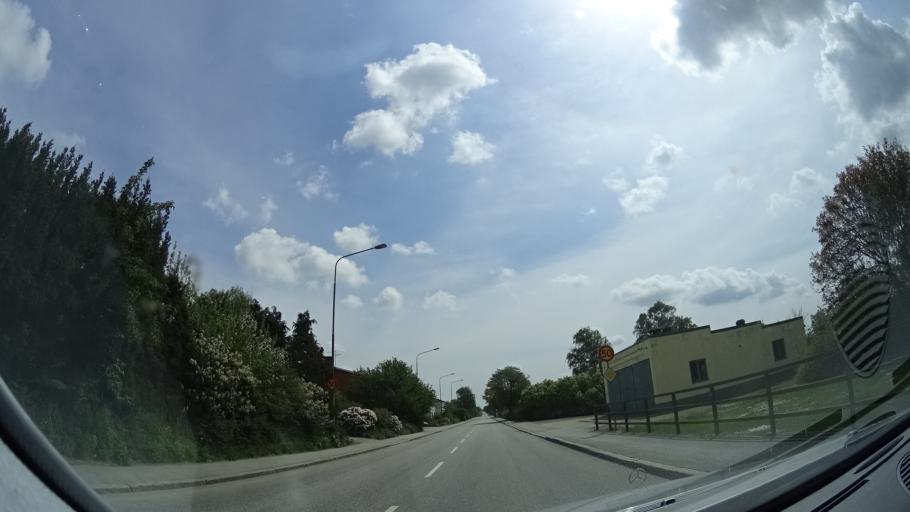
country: SE
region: Skane
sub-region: Hoors Kommun
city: Loberod
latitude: 55.7174
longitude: 13.5248
